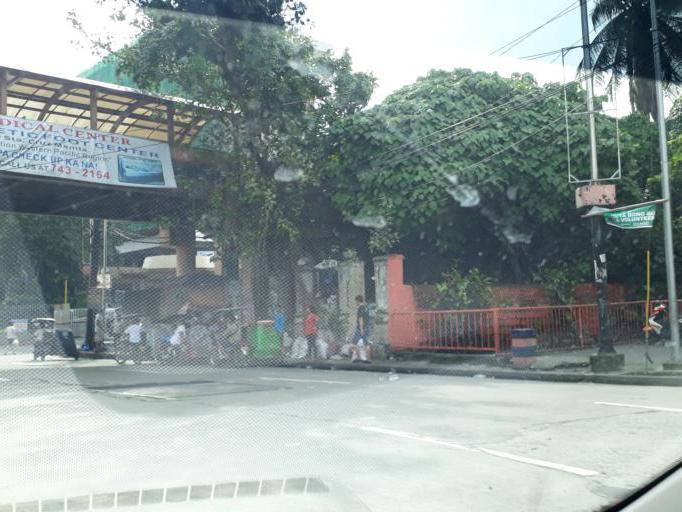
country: PH
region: Metro Manila
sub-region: City of Manila
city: Manila
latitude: 14.6259
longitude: 120.9890
